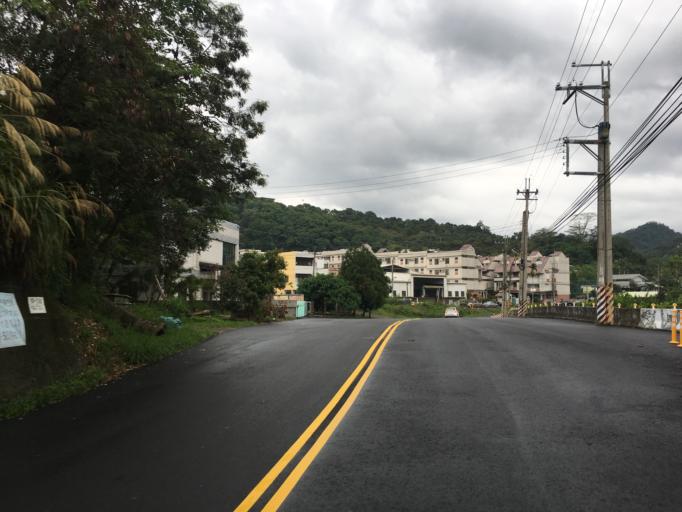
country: TW
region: Taiwan
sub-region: Taichung City
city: Taichung
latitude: 24.0678
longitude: 120.7343
